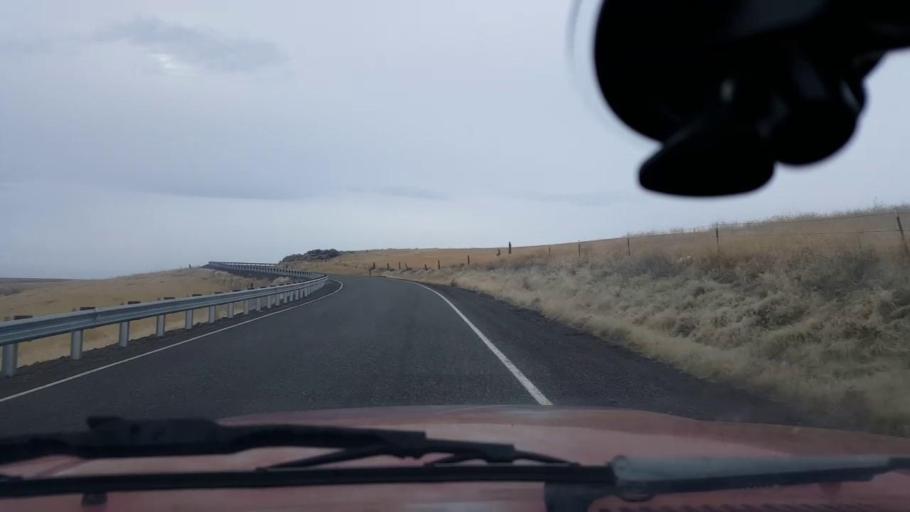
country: US
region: Washington
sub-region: Asotin County
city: Clarkston Heights-Vineland
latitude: 46.3345
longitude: -117.3074
